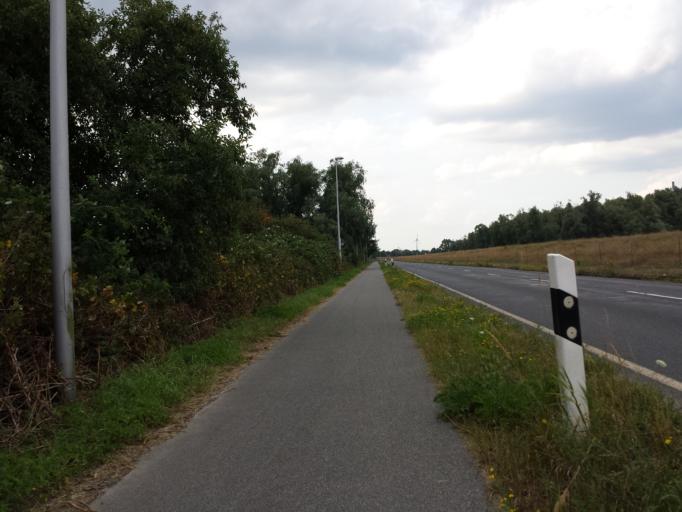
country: DE
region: Lower Saxony
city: Stuhr
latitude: 53.1011
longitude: 8.7253
